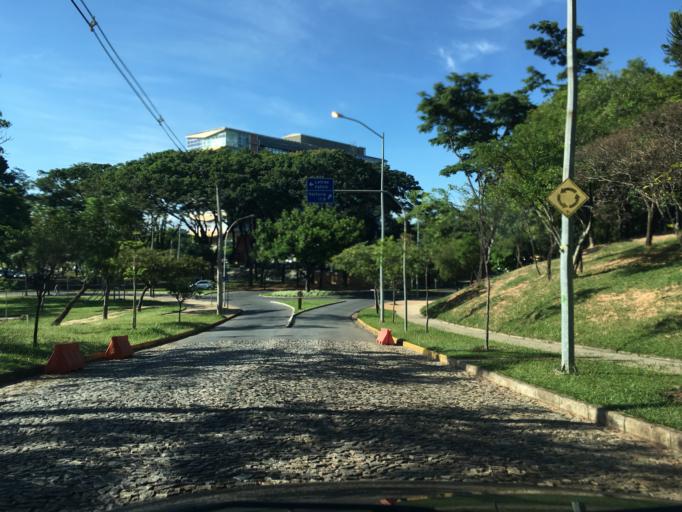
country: BR
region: Minas Gerais
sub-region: Belo Horizonte
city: Belo Horizonte
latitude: -19.8644
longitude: -43.9643
